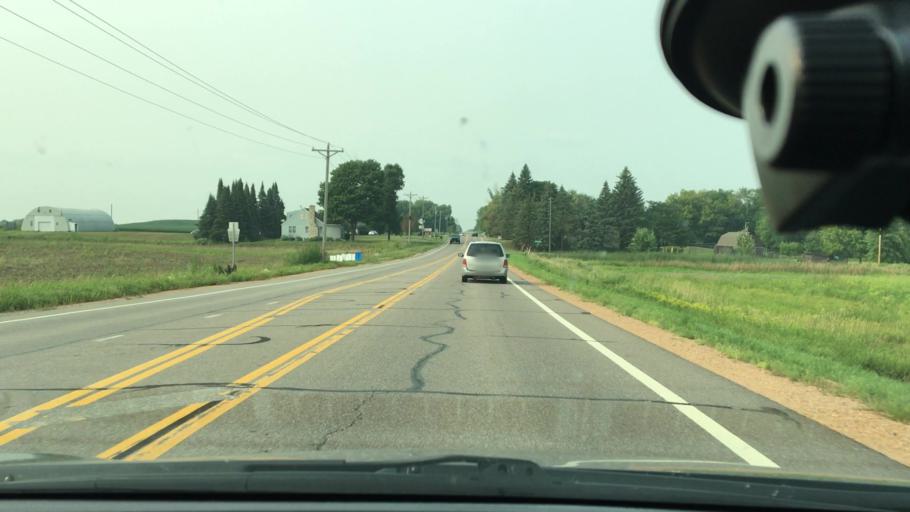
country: US
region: Minnesota
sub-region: Hennepin County
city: Osseo
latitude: 45.1570
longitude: -93.4620
